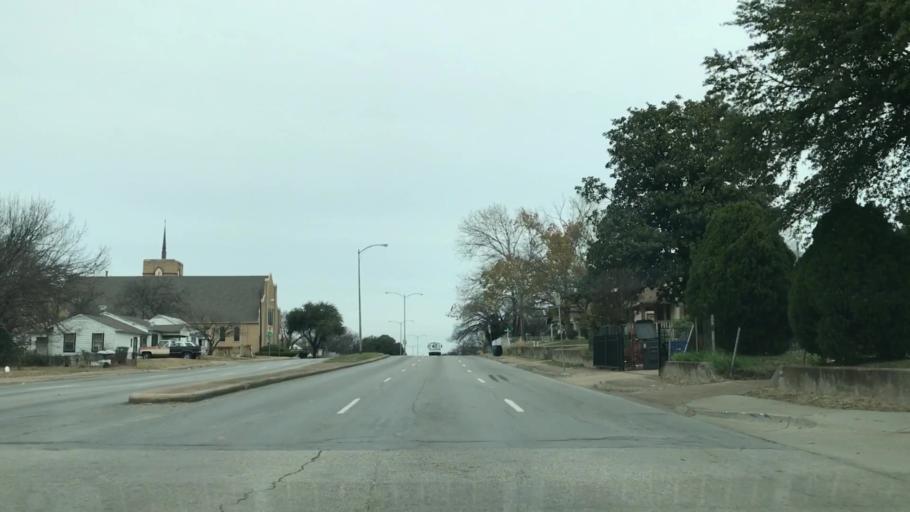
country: US
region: Texas
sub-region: Dallas County
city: Dallas
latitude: 32.7168
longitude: -96.8145
